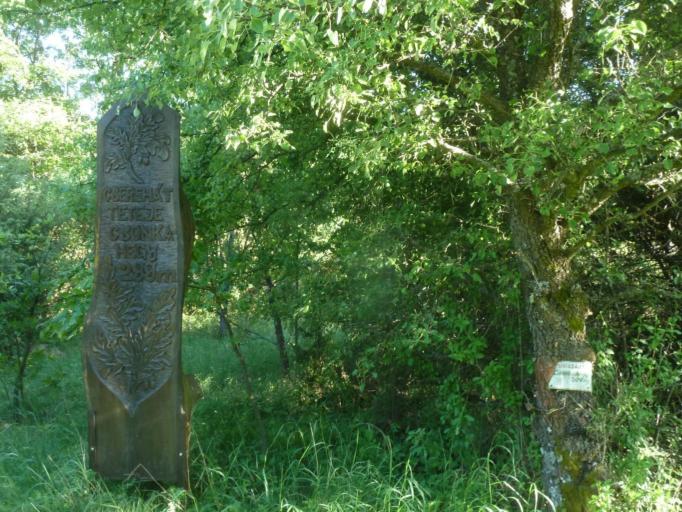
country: SK
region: Kosicky
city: Moldava nad Bodvou
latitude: 48.5156
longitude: 20.9489
